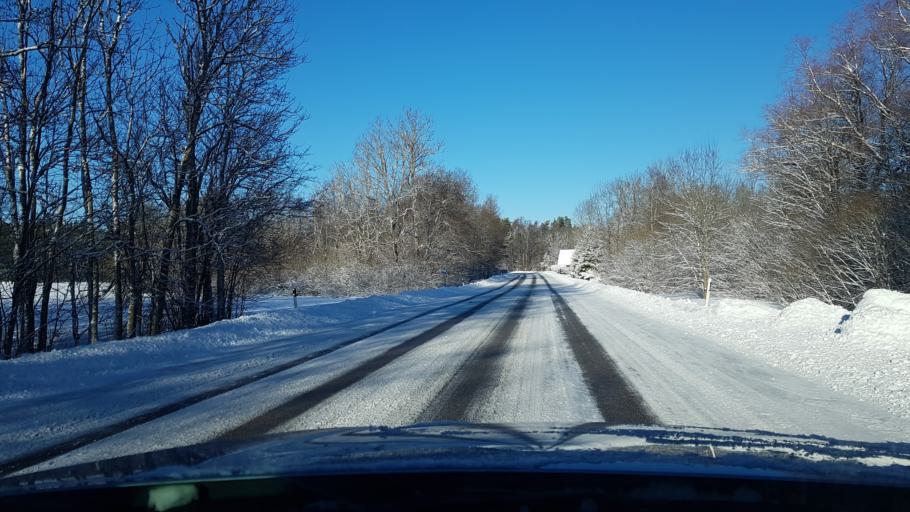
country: EE
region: Hiiumaa
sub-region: Kaerdla linn
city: Kardla
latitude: 58.9197
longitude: 22.7944
